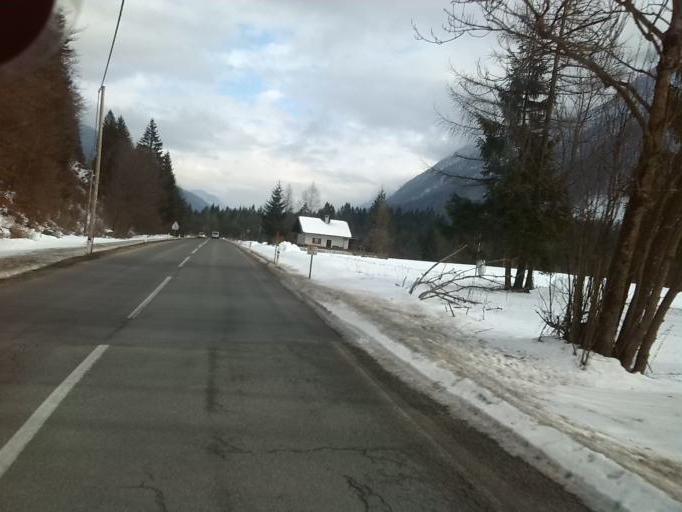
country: SI
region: Kranjska Gora
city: Mojstrana
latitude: 46.4805
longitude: 13.8603
